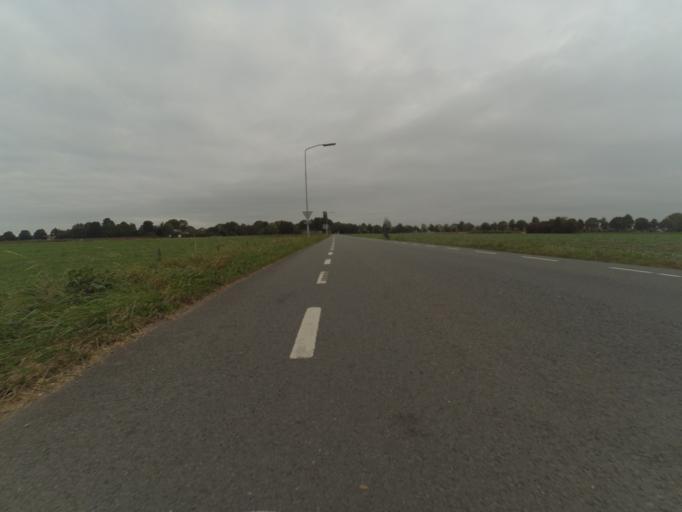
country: NL
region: Utrecht
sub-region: Gemeente Wijk bij Duurstede
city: Wijk bij Duurstede
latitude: 51.9373
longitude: 5.3113
